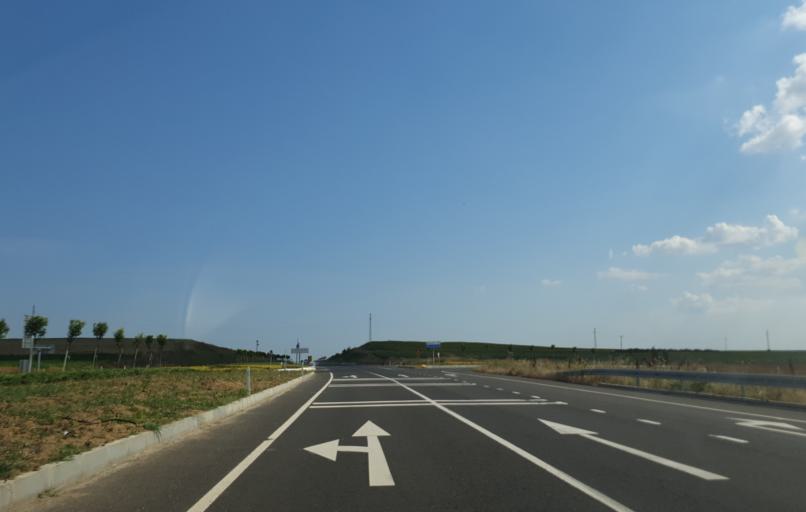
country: TR
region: Tekirdag
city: Muratli
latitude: 41.2117
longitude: 27.5341
